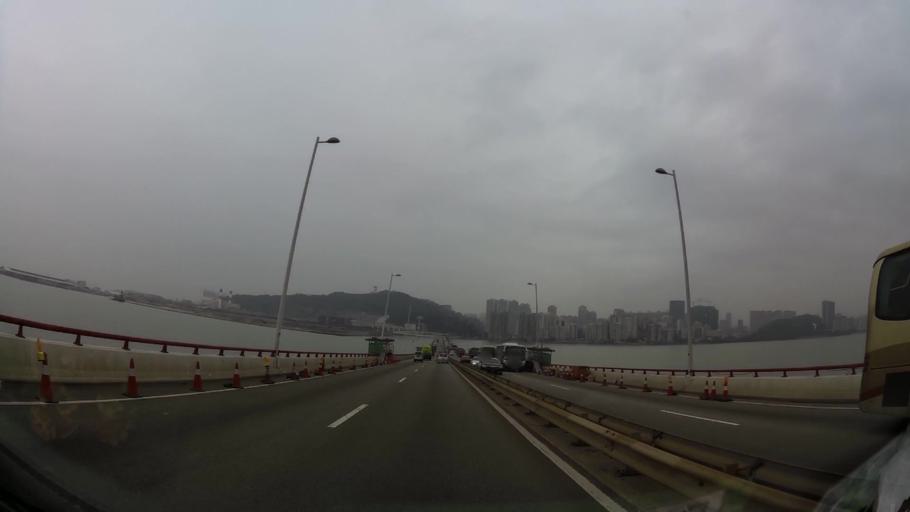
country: MO
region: Macau
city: Macau
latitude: 22.1753
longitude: 113.5635
